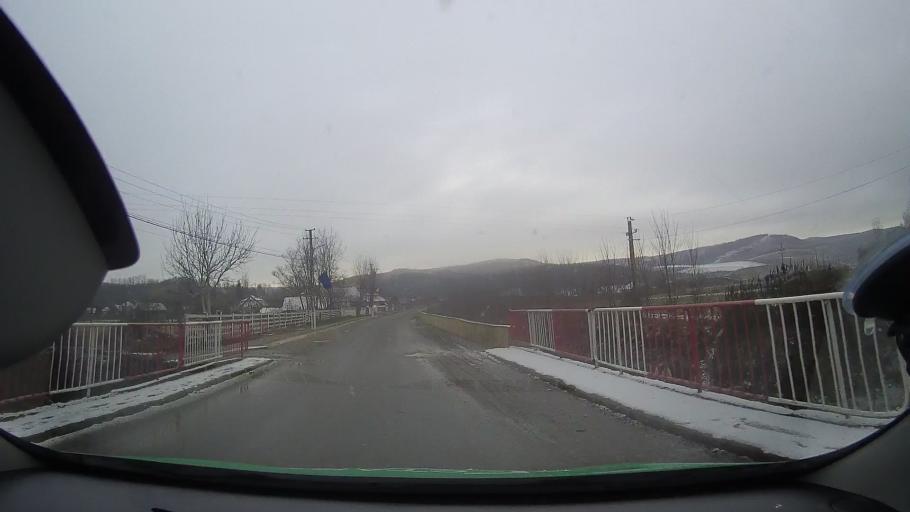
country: RO
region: Alba
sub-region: Comuna Farau
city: Farau
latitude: 46.3392
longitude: 24.0051
